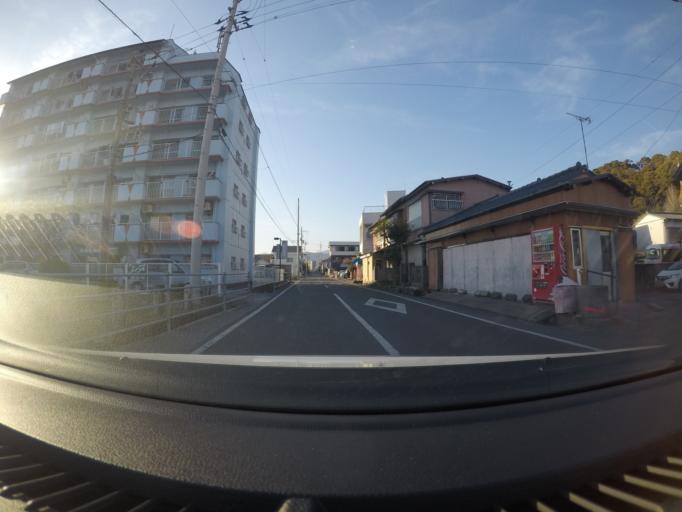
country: JP
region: Kochi
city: Kochi-shi
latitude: 33.5462
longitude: 133.5700
